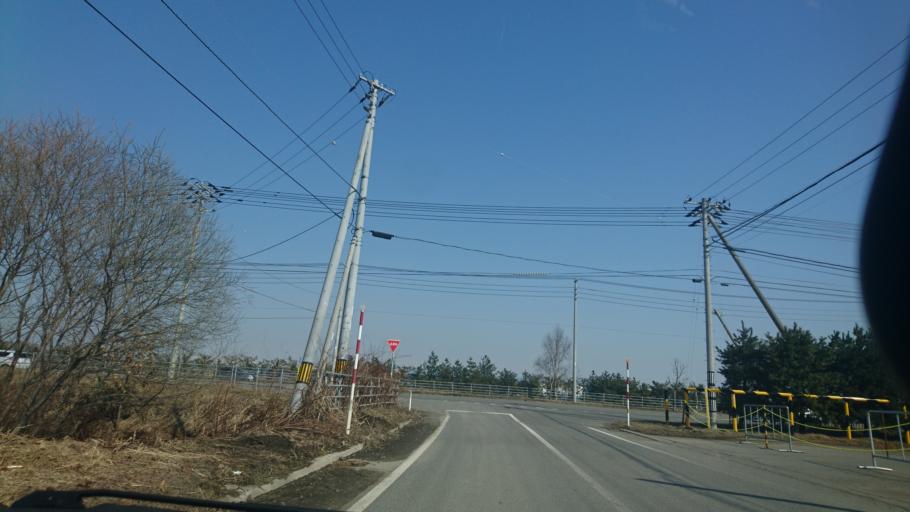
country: JP
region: Hokkaido
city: Obihiro
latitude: 42.9221
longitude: 143.0722
